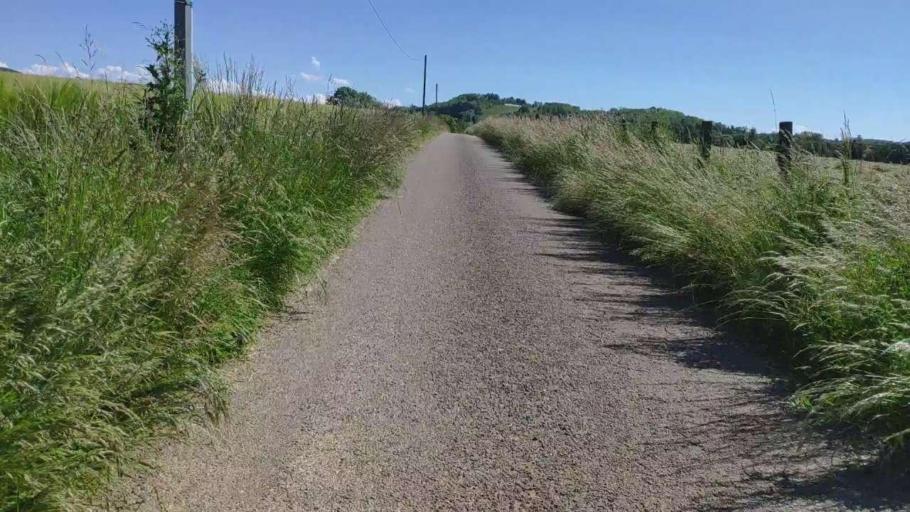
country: FR
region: Franche-Comte
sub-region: Departement du Jura
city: Perrigny
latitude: 46.7364
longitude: 5.5835
